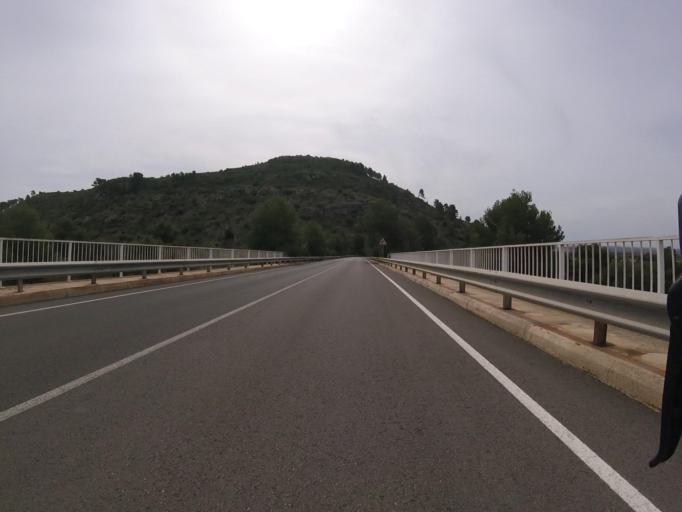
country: ES
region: Valencia
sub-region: Provincia de Castello
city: Benicassim
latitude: 40.0599
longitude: 0.0455
